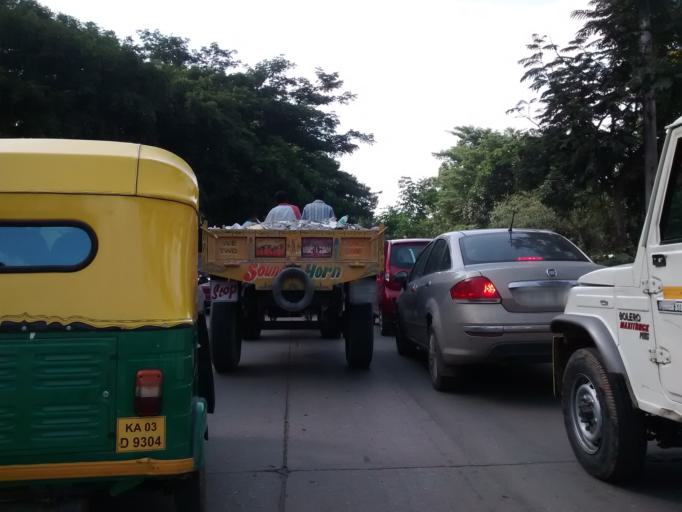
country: IN
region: Karnataka
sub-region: Bangalore Urban
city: Bangalore
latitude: 12.9849
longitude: 77.6485
